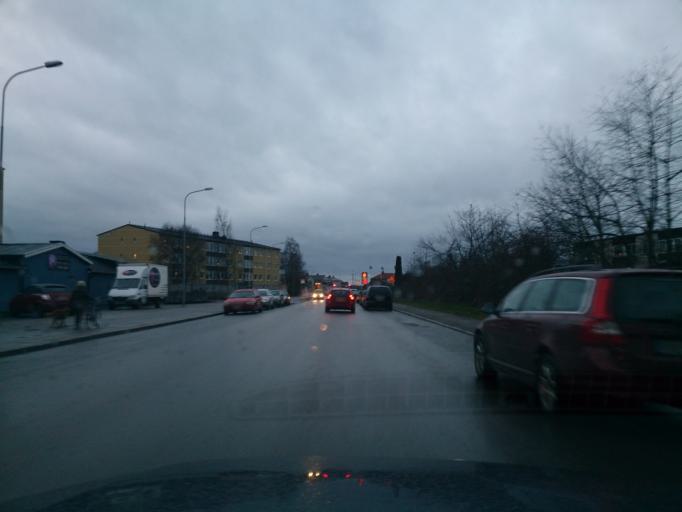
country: SE
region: OEstergoetland
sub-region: Norrkopings Kommun
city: Norrkoping
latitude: 58.6079
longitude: 16.1435
